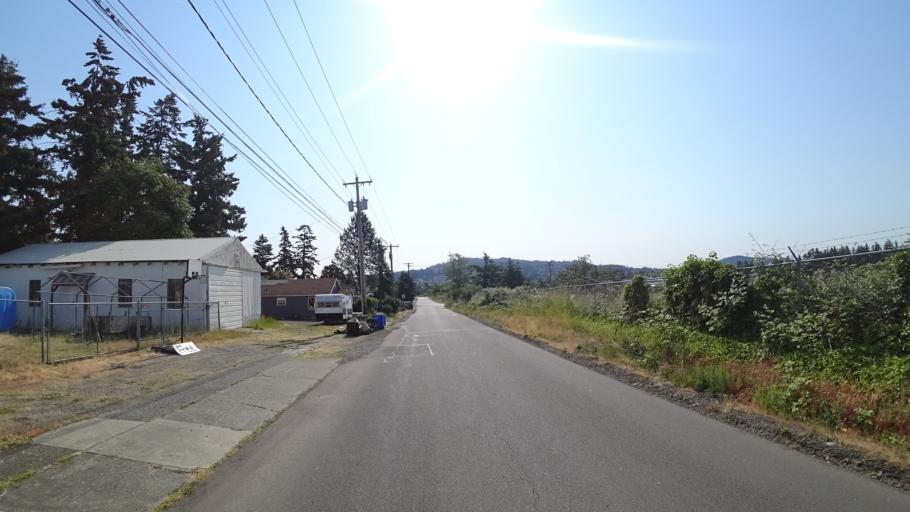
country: US
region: Oregon
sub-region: Multnomah County
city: Lents
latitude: 45.4586
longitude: -122.5941
